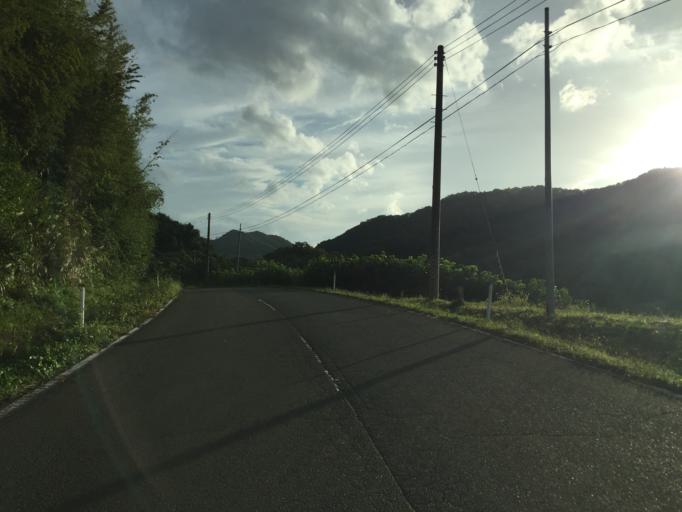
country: JP
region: Fukushima
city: Yanagawamachi-saiwaicho
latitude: 37.9113
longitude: 140.6656
